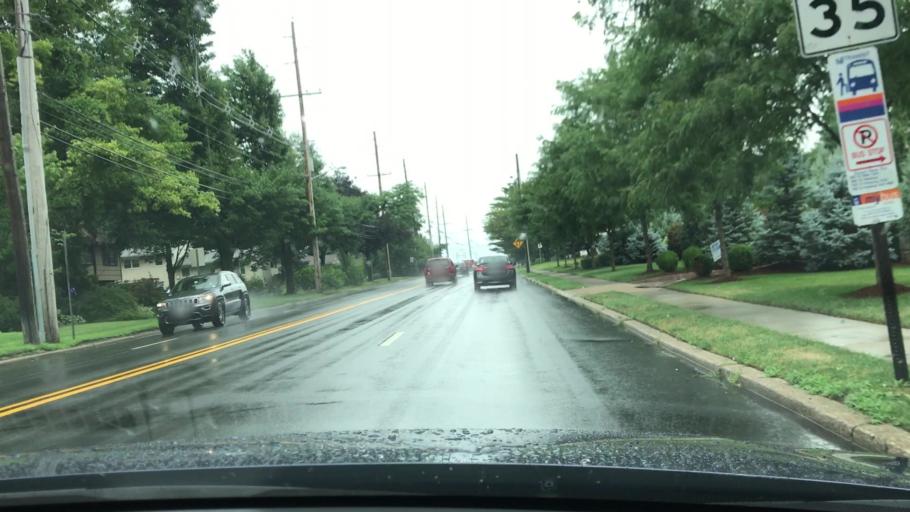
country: US
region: New Jersey
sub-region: Bergen County
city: Paramus
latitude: 40.9621
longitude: -74.0610
